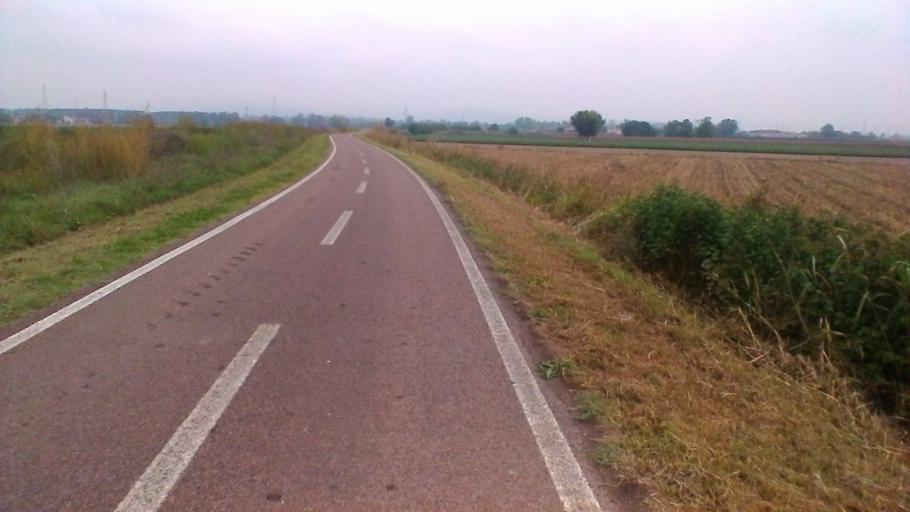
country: IT
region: Veneto
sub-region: Provincia di Verona
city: Campagnola
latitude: 45.3856
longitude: 11.0708
